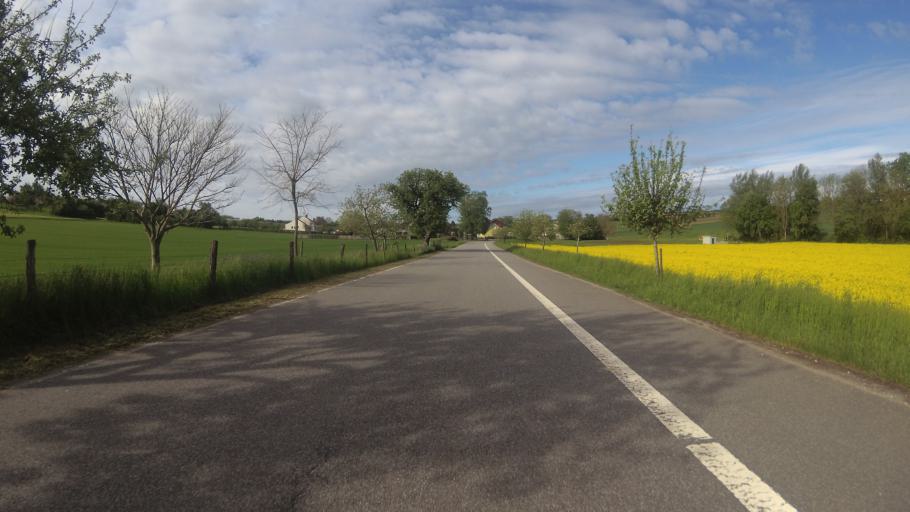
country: DE
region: Saarland
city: Perl
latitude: 49.4795
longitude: 6.4488
